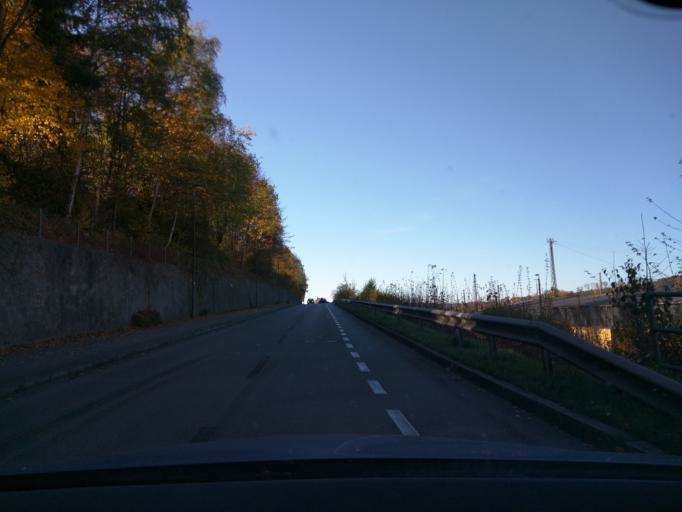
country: DE
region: Bavaria
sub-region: Lower Bavaria
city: Passau
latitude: 48.5722
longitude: 13.4360
